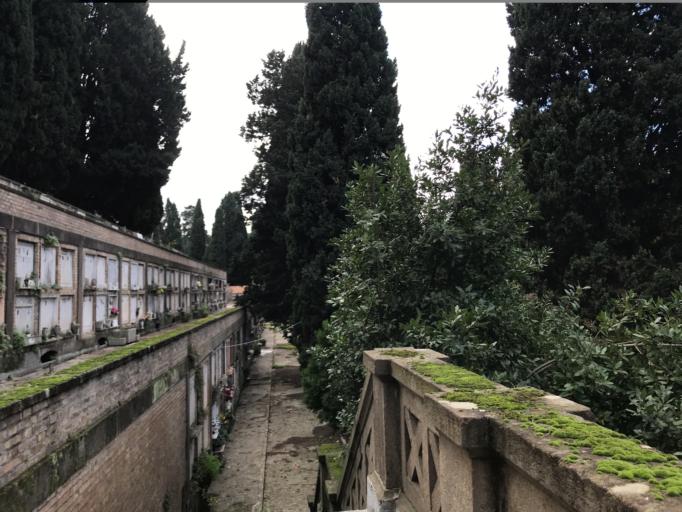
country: IT
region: Latium
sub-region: Citta metropolitana di Roma Capitale
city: Rome
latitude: 41.9057
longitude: 12.5234
